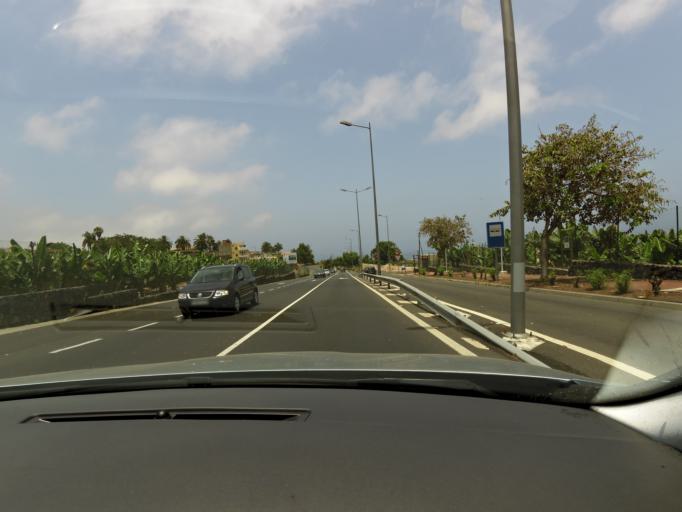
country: ES
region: Canary Islands
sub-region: Provincia de Santa Cruz de Tenerife
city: La Orotava
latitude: 28.4057
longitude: -16.5275
